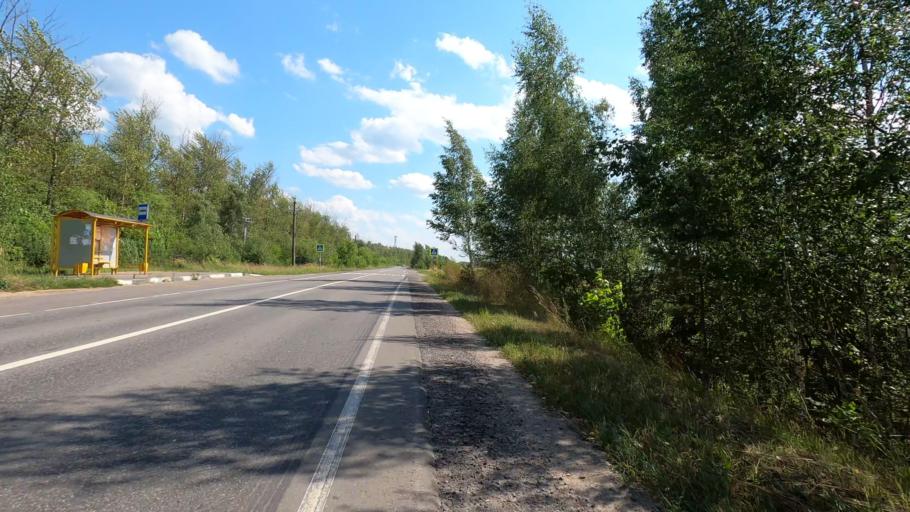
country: RU
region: Moskovskaya
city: Peski
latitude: 55.2338
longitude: 38.7637
